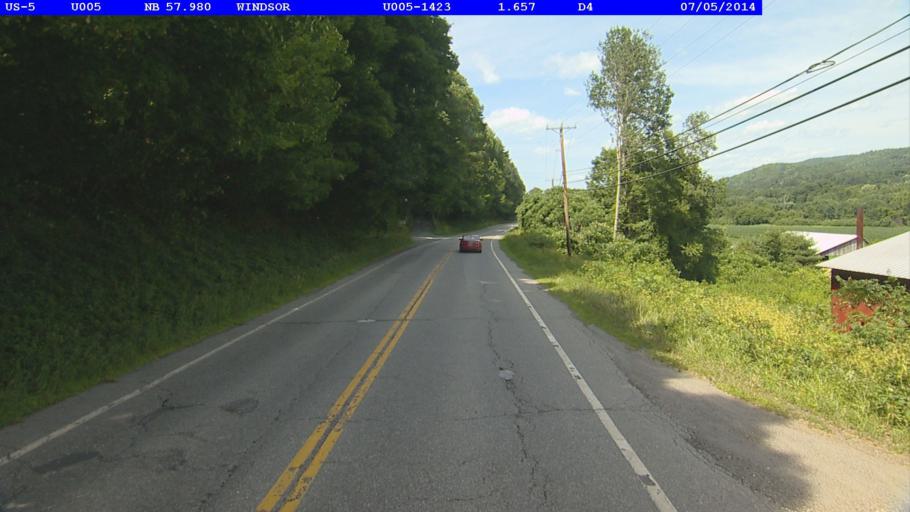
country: US
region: Vermont
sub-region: Windsor County
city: Windsor
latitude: 43.4521
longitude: -72.3951
